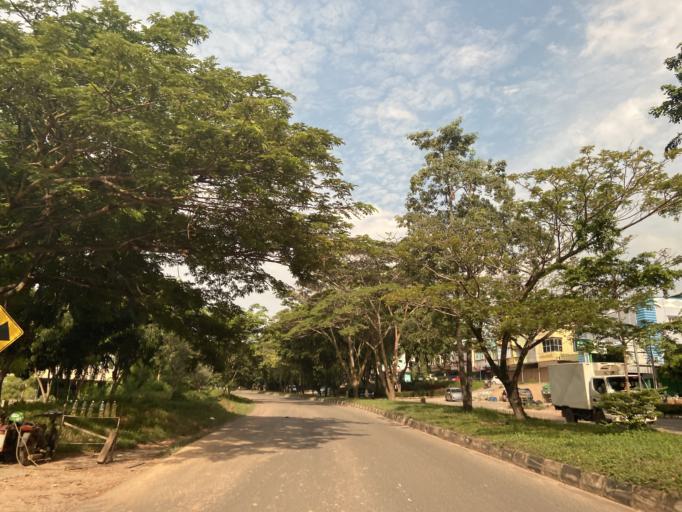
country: SG
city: Singapore
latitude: 1.1047
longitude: 104.0675
